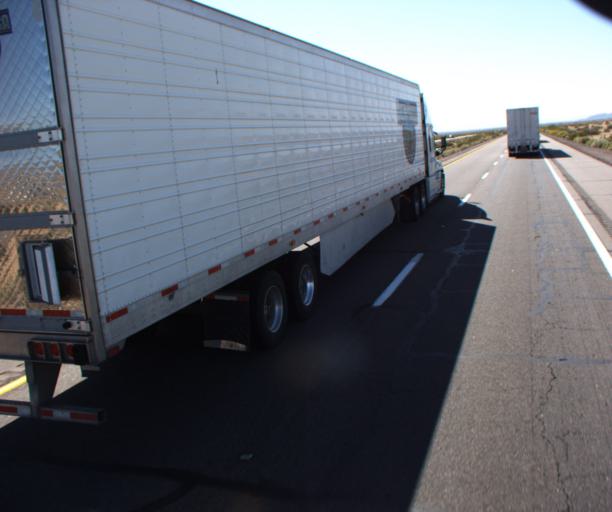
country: US
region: Arizona
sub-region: Yuma County
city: Wellton
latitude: 32.7151
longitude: -113.8125
